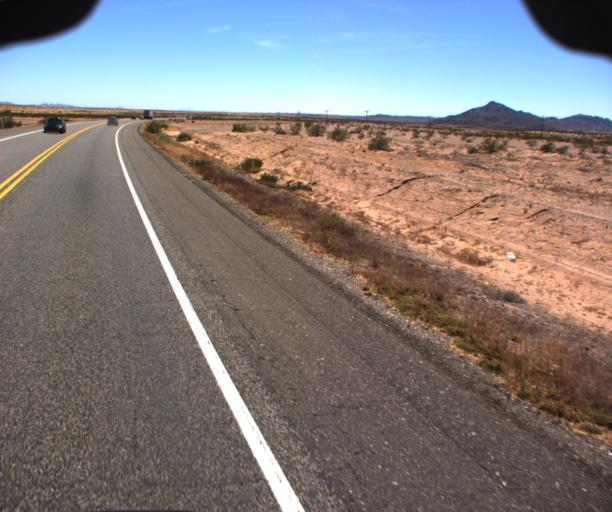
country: US
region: Arizona
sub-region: La Paz County
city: Parker
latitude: 34.0685
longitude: -114.2587
